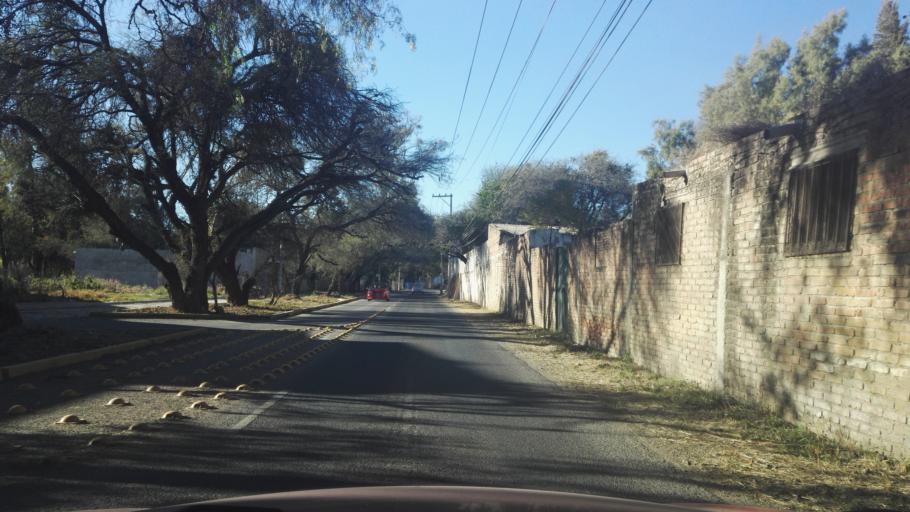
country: MX
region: Guanajuato
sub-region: Leon
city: Ladrilleras del Refugio
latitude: 21.0680
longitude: -101.5973
